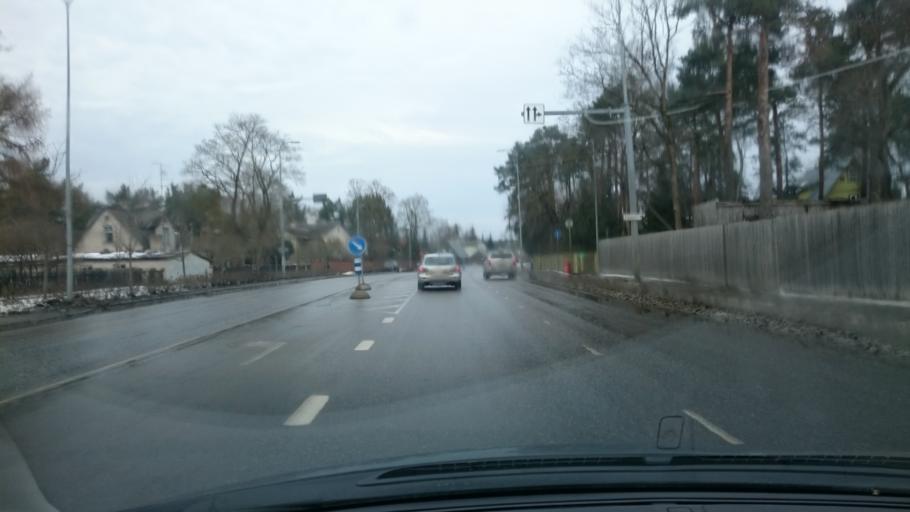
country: EE
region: Harju
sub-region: Tallinna linn
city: Tallinn
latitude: 59.3851
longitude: 24.7176
